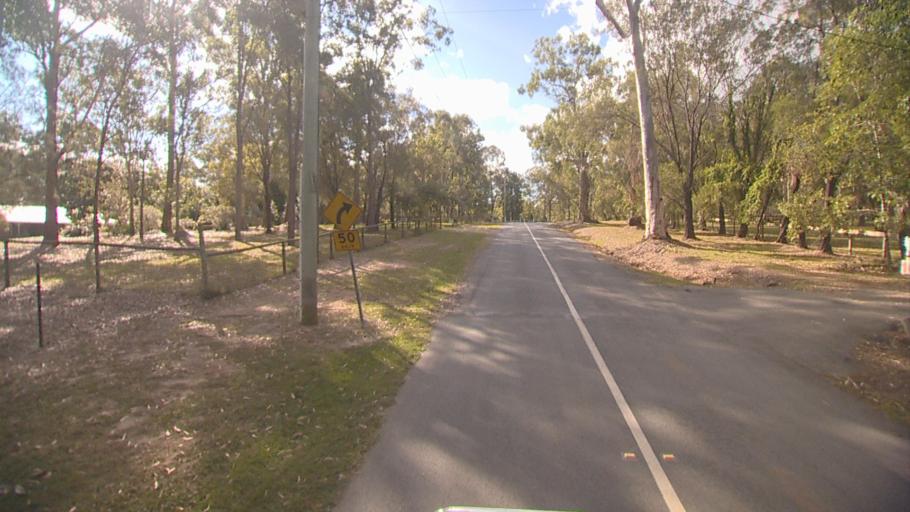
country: AU
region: Queensland
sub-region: Gold Coast
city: Yatala
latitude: -27.6597
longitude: 153.2416
